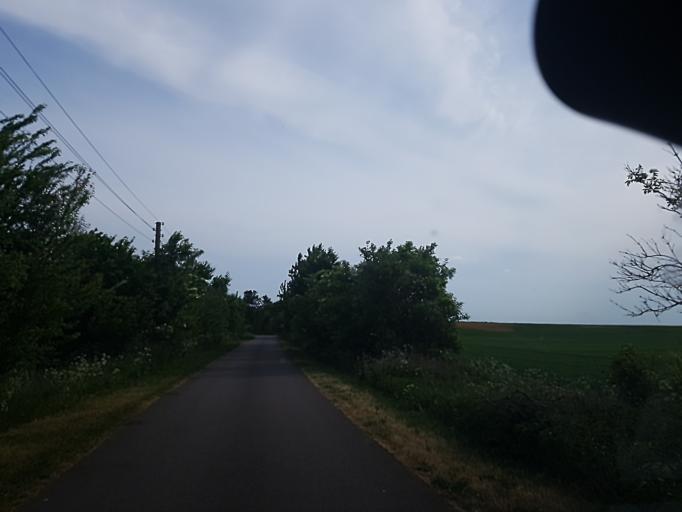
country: DE
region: Brandenburg
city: Niemegk
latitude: 52.0142
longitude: 12.6627
